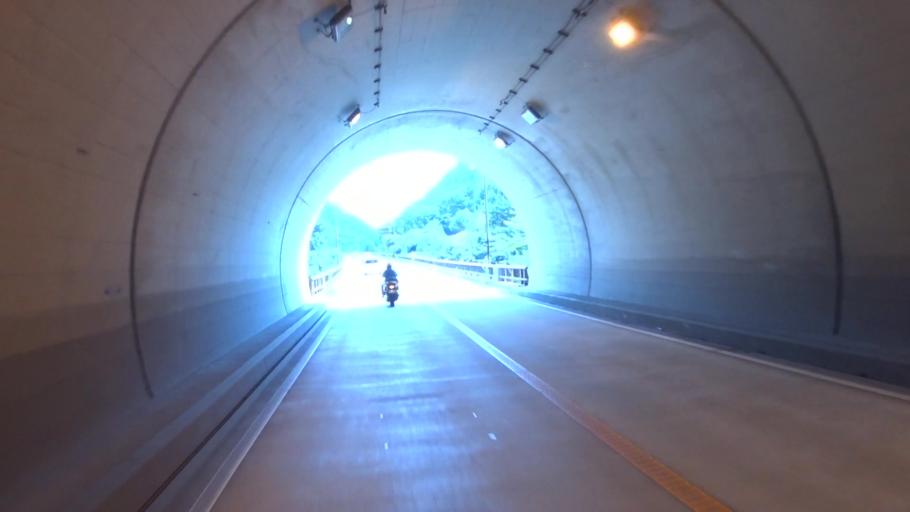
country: JP
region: Kyoto
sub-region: Kyoto-shi
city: Kamigyo-ku
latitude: 35.0756
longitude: 135.6858
